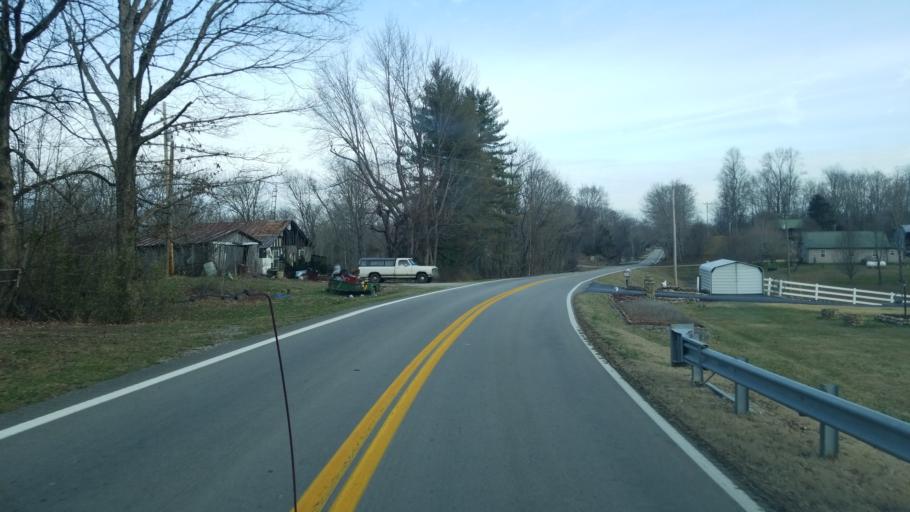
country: US
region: Kentucky
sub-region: Clinton County
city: Albany
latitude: 36.8272
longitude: -85.1997
